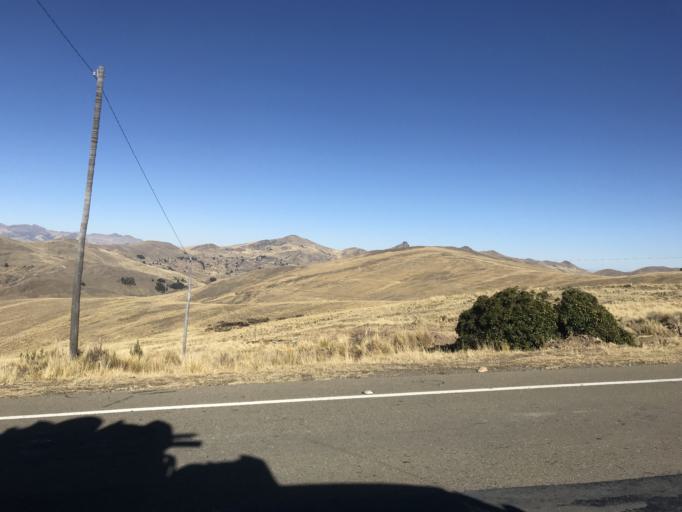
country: PE
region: Puno
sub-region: Yunguyo
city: Yunguyo
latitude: -16.1690
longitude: -68.9843
